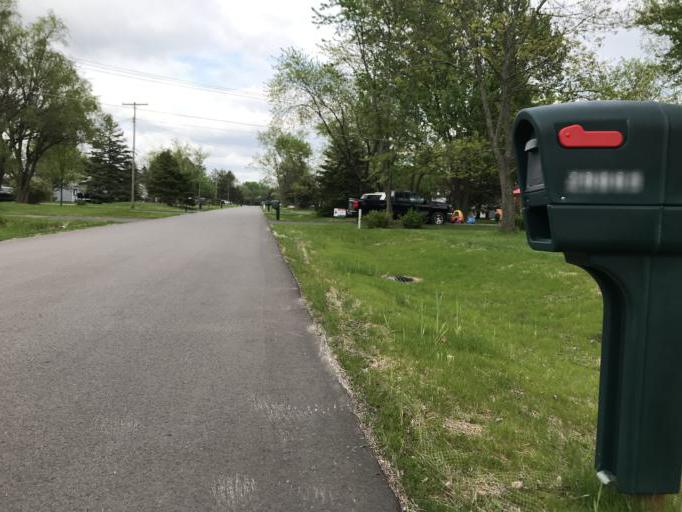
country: US
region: Michigan
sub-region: Oakland County
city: Farmington
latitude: 42.4758
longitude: -83.3424
